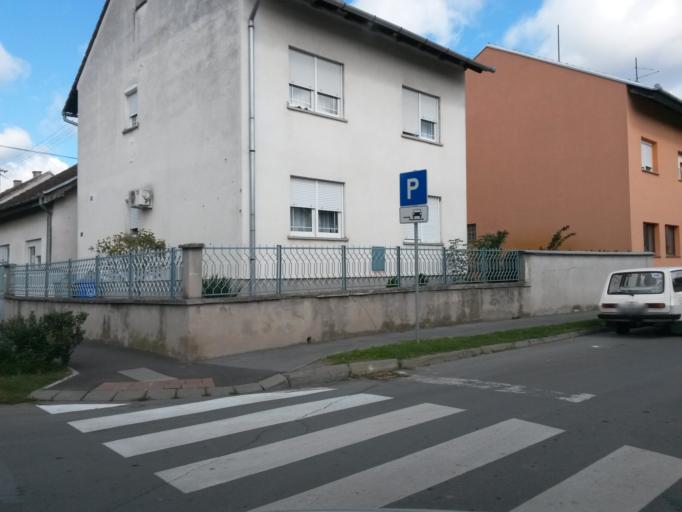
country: HR
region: Osjecko-Baranjska
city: Visnjevac
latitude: 45.5611
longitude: 18.6478
